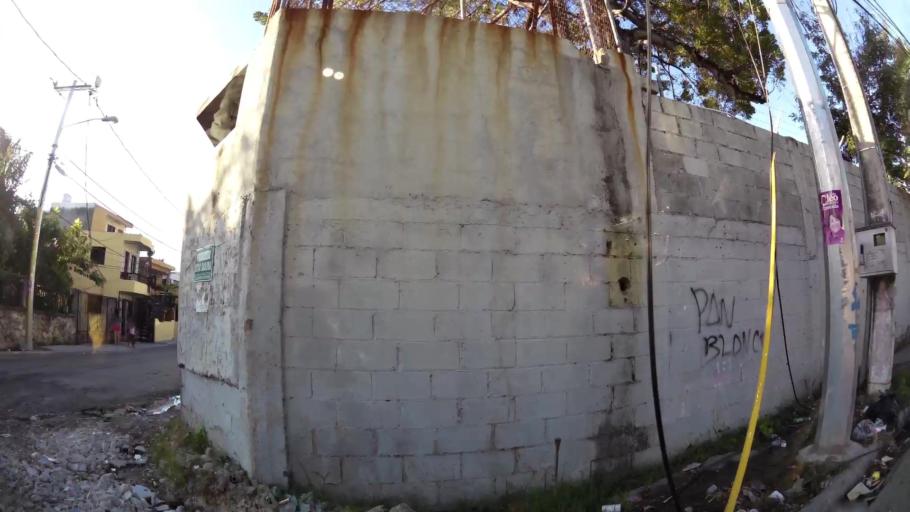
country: DO
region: Nacional
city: Santo Domingo
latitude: 18.4861
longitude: -69.9702
